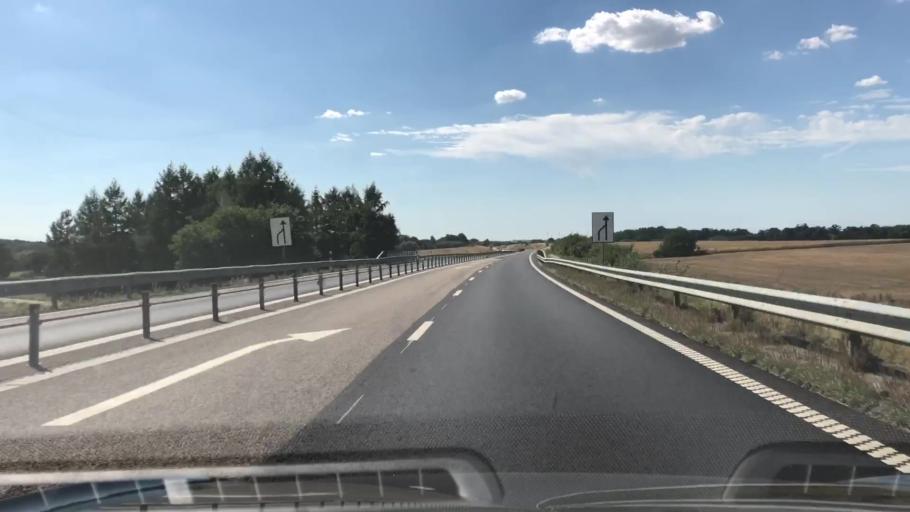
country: SE
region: Skane
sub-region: Horby Kommun
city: Hoerby
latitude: 55.8520
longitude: 13.6215
